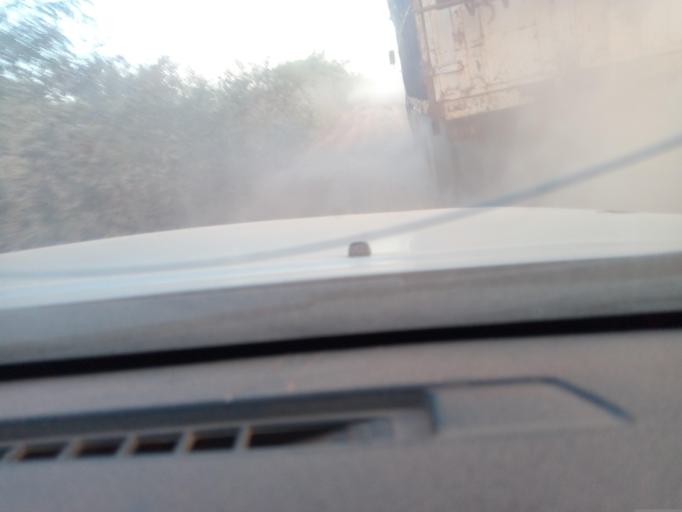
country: ML
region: Koulikoro
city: Dioila
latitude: 12.1584
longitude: -6.1713
